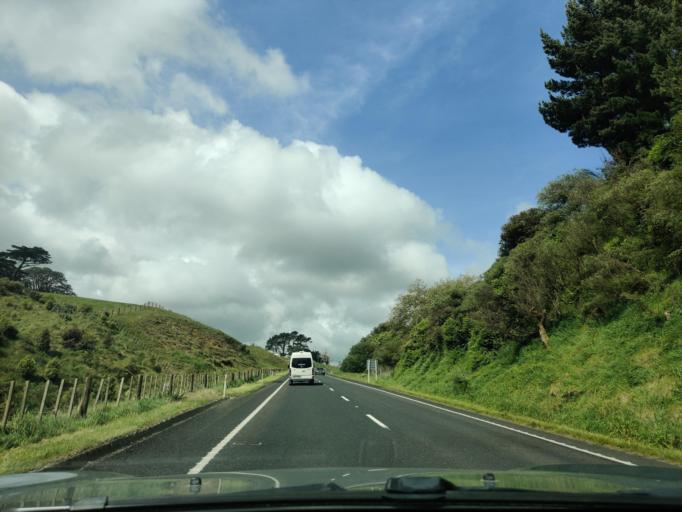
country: NZ
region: Manawatu-Wanganui
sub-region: Wanganui District
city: Wanganui
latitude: -39.8236
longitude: 174.8427
